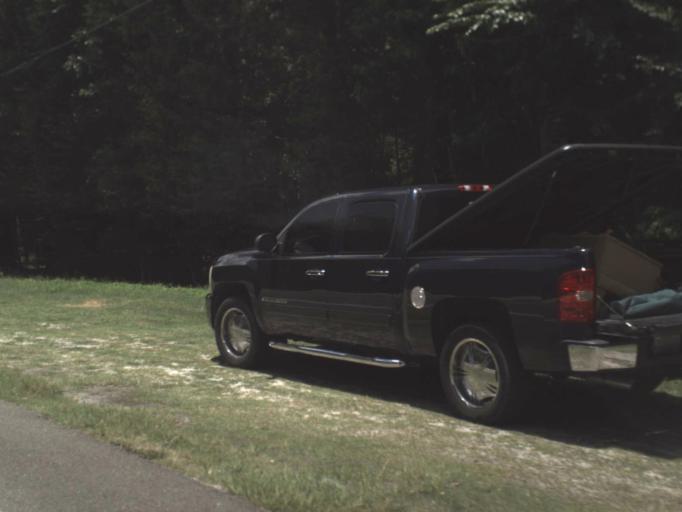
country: US
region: Florida
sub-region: Alachua County
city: Gainesville
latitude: 29.6879
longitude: -82.2208
